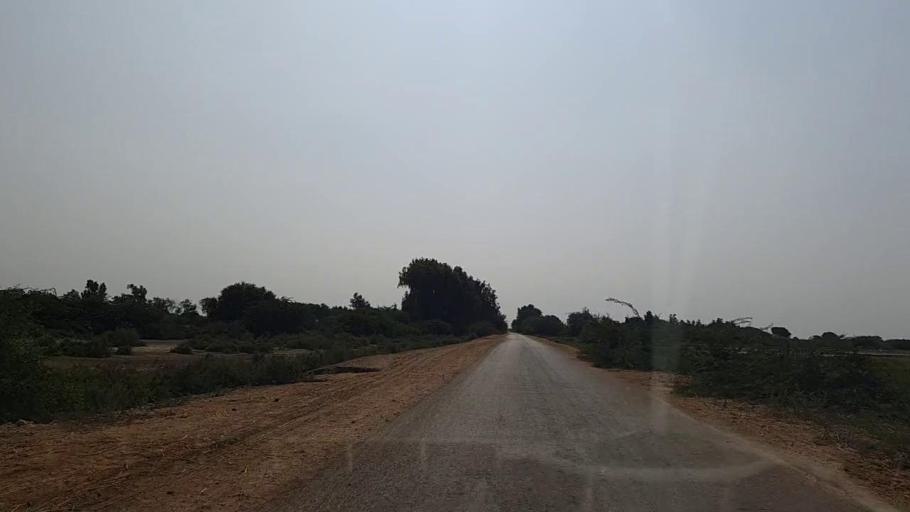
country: PK
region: Sindh
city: Chuhar Jamali
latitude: 24.2474
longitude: 67.9049
